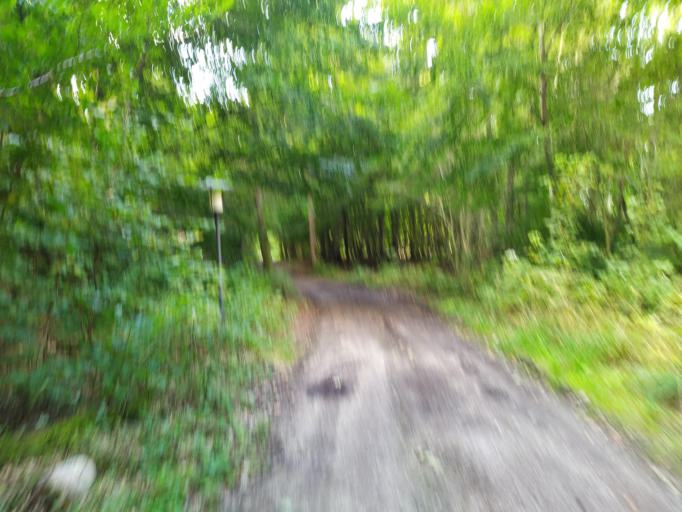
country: DK
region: Capital Region
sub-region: Egedal Kommune
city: Ganlose
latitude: 55.8116
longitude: 12.2736
